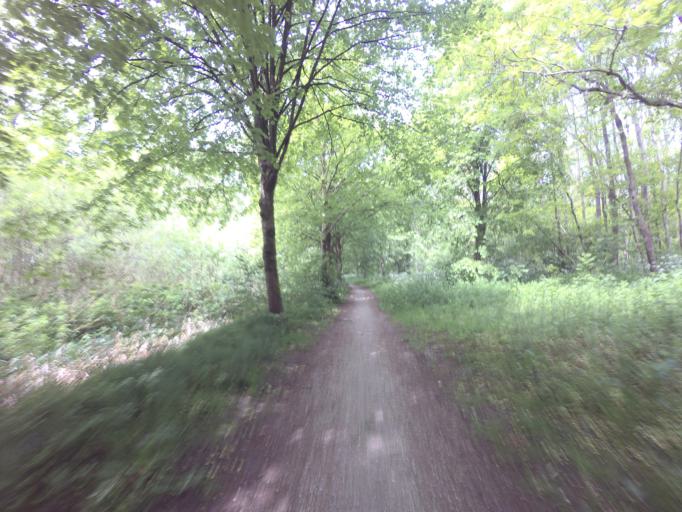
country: NL
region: Friesland
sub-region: Sudwest Fryslan
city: Bolsward
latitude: 53.0957
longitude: 5.4748
